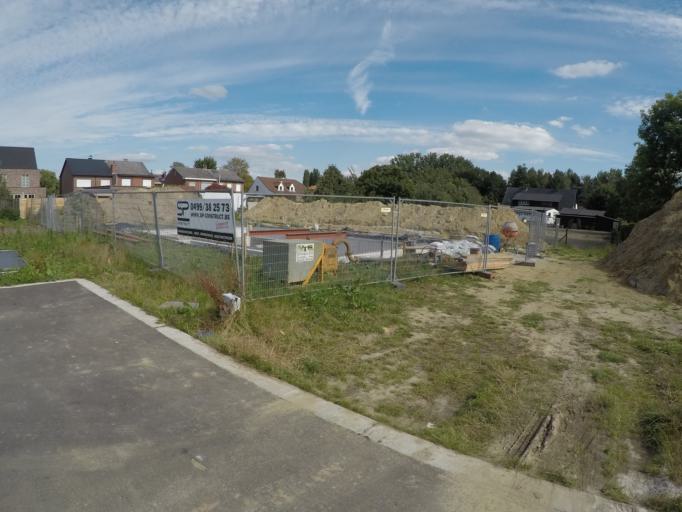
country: BE
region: Flanders
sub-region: Provincie Antwerpen
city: Lier
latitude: 51.1465
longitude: 4.6175
